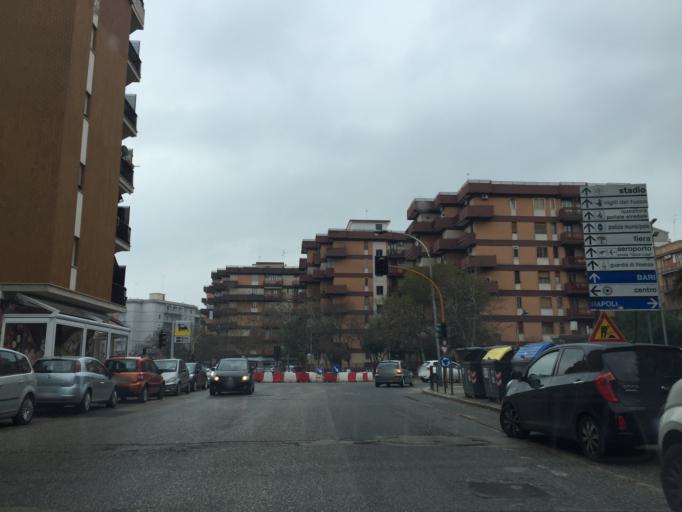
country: IT
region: Apulia
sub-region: Provincia di Foggia
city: Foggia
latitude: 41.4595
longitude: 15.5347
